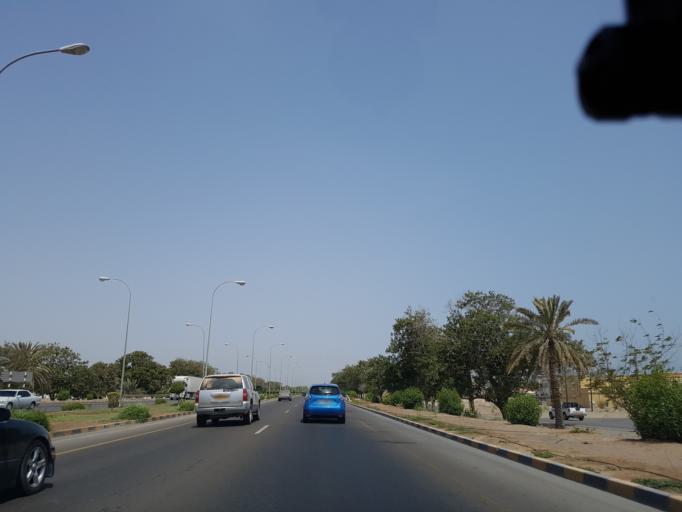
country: OM
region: Al Batinah
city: Saham
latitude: 24.2433
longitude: 56.8180
